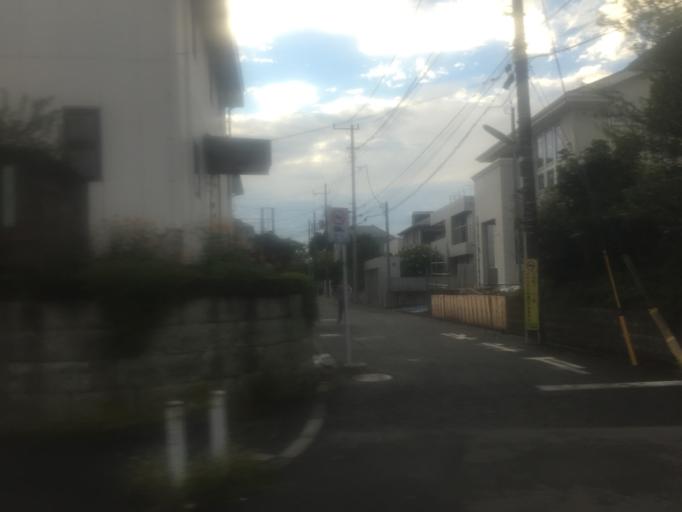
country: JP
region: Tokyo
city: Tokyo
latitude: 35.6004
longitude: 139.6643
